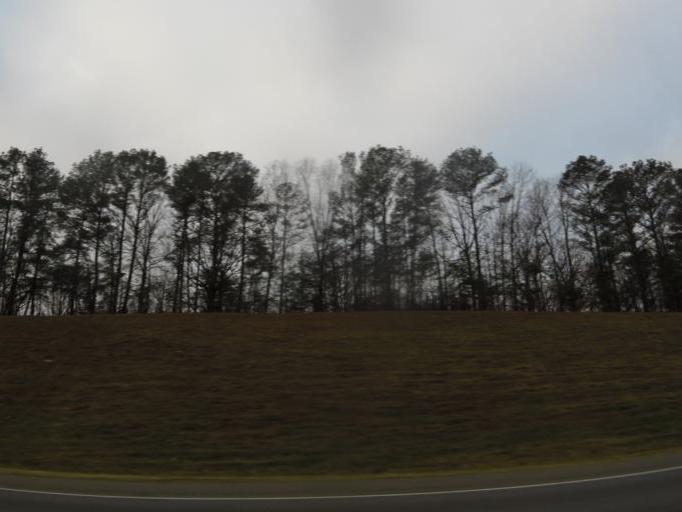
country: US
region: Alabama
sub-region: Jefferson County
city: Fultondale
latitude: 33.6240
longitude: -86.8185
